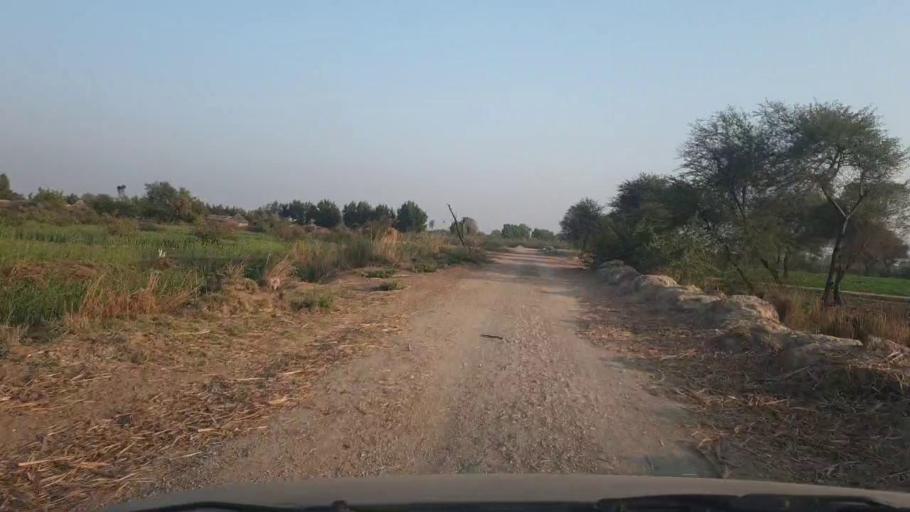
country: PK
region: Sindh
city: Mirwah Gorchani
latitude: 25.3616
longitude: 69.1522
